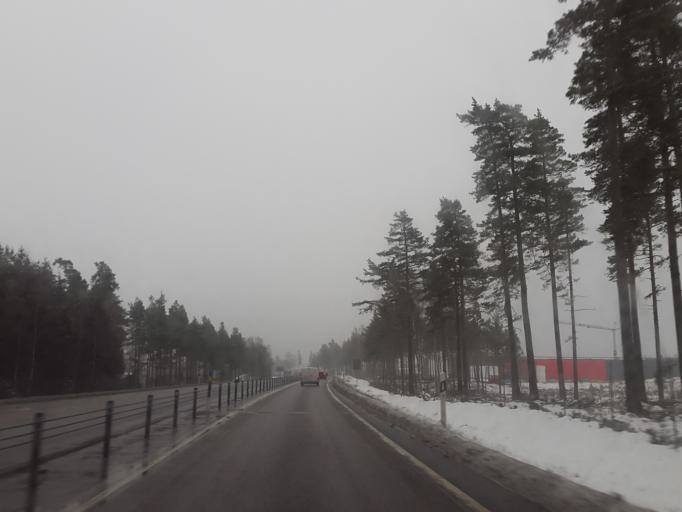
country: SE
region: Joenkoeping
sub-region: Jonkopings Kommun
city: Jonkoping
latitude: 57.7708
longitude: 14.0843
